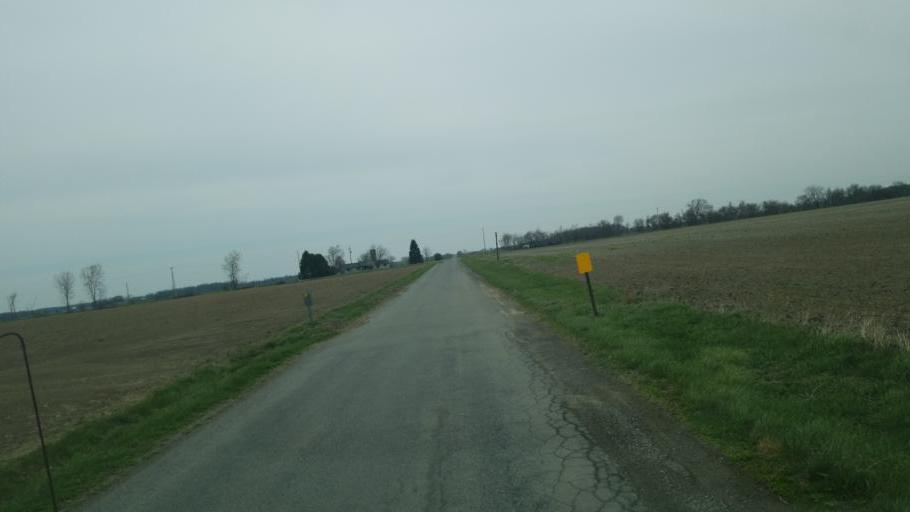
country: US
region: Ohio
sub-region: Hardin County
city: Forest
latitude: 40.9168
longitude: -83.5144
